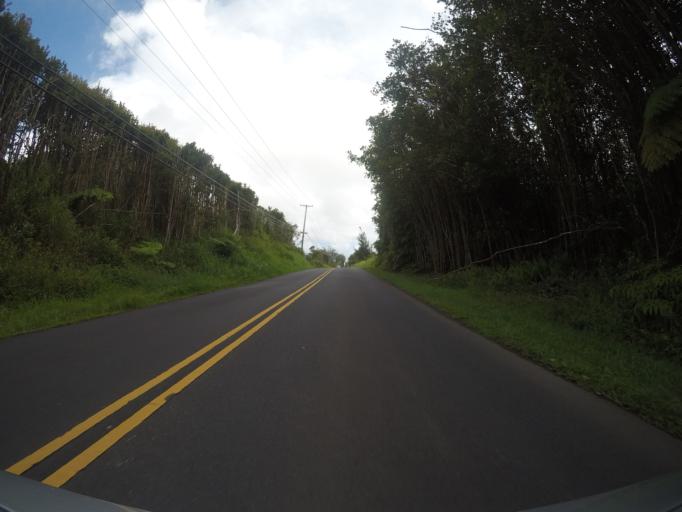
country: US
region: Hawaii
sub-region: Hawaii County
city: Fern Acres
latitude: 19.4836
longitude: -155.1487
